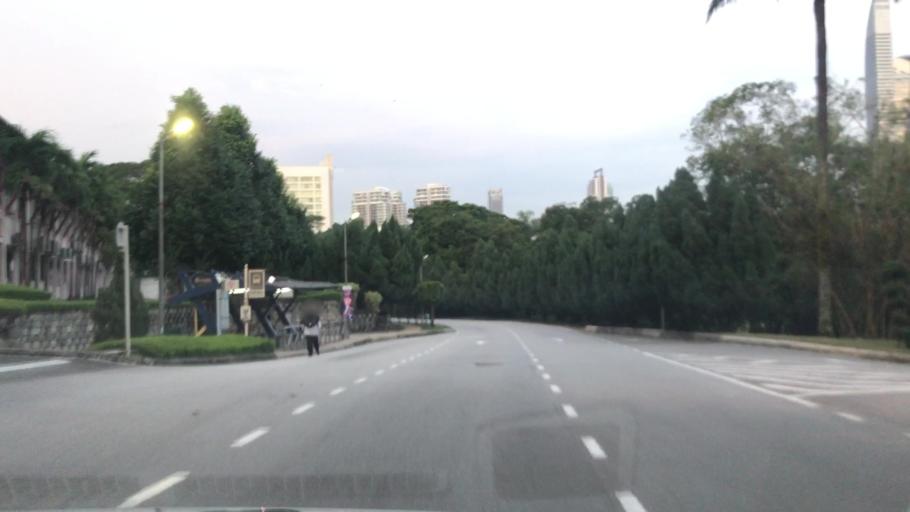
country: MY
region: Kuala Lumpur
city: Kuala Lumpur
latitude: 3.1217
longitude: 101.6581
